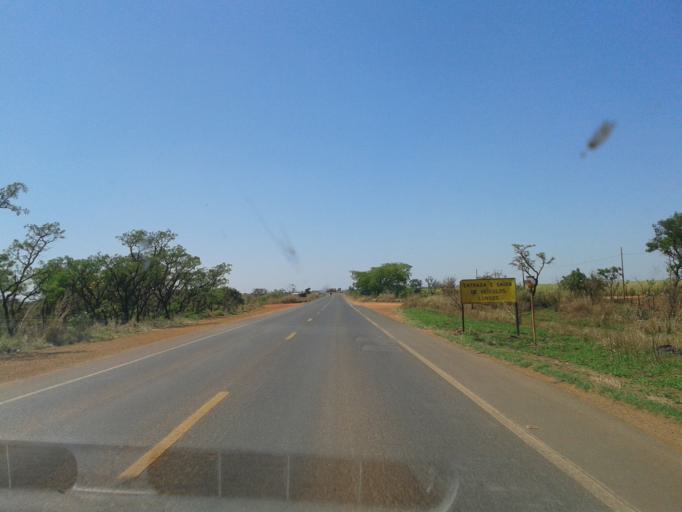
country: BR
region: Minas Gerais
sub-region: Sacramento
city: Sacramento
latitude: -19.3202
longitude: -47.5642
